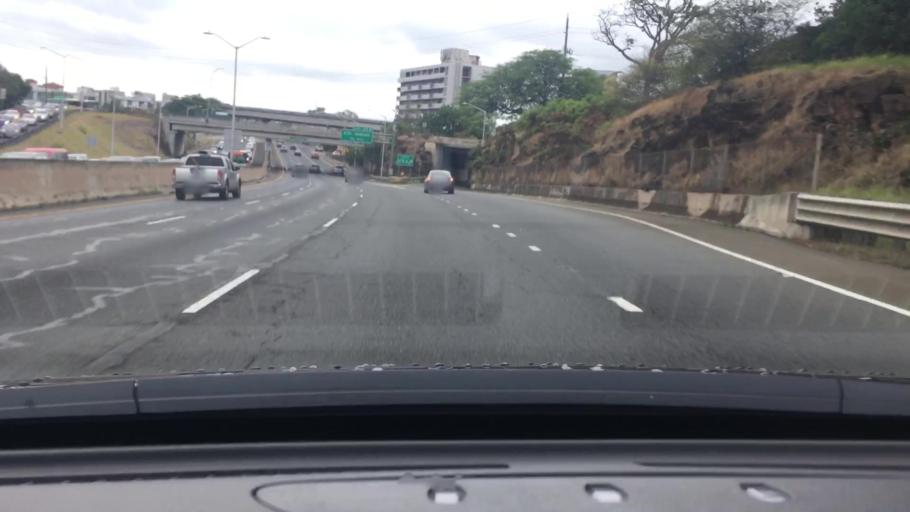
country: US
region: Hawaii
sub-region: Honolulu County
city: Honolulu
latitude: 21.2913
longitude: -157.8184
